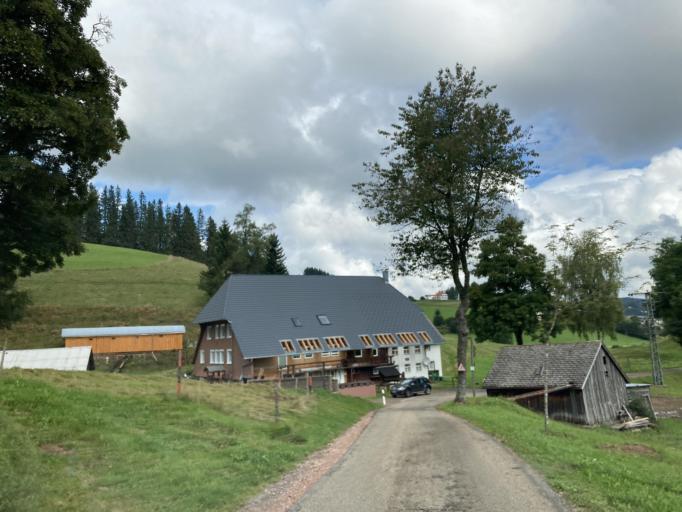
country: DE
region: Baden-Wuerttemberg
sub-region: Freiburg Region
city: Furtwangen im Schwarzwald
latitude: 48.0334
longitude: 8.1865
